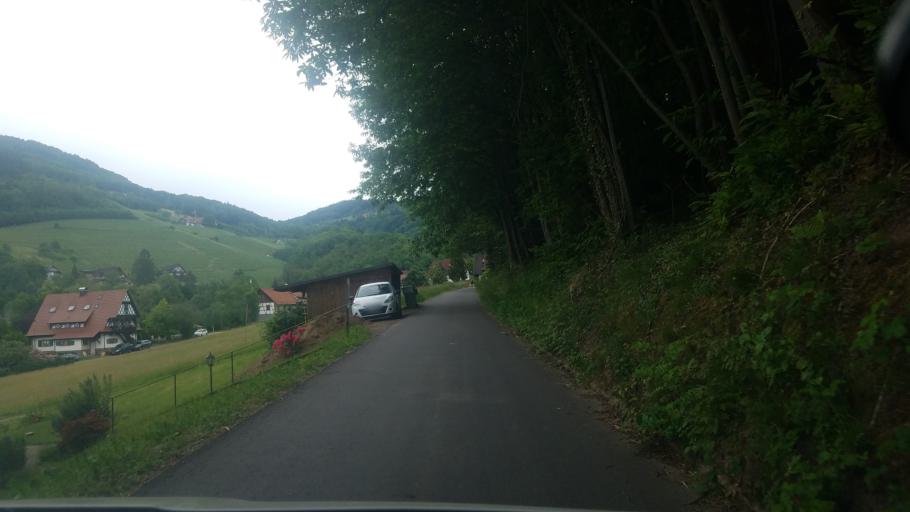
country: DE
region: Baden-Wuerttemberg
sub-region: Freiburg Region
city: Sasbachwalden
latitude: 48.6158
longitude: 8.1272
